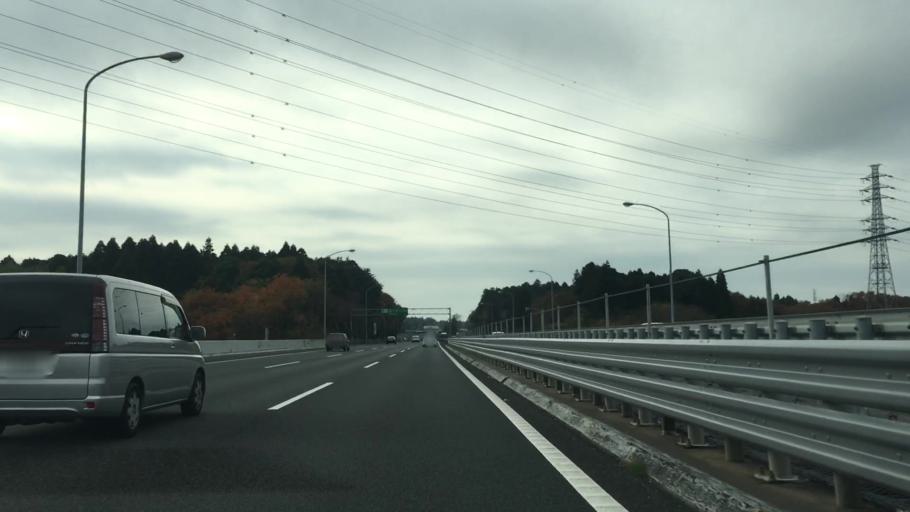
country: JP
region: Chiba
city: Shisui
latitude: 35.7391
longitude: 140.3056
